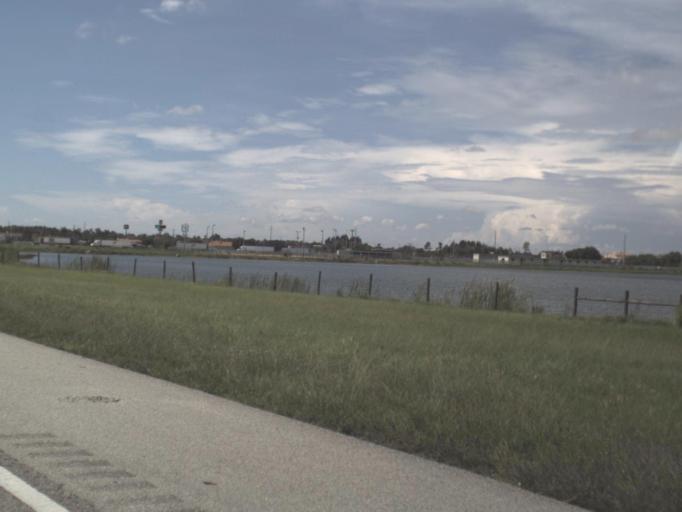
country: US
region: Florida
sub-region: Charlotte County
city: Charlotte Park
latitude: 26.9015
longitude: -82.0078
